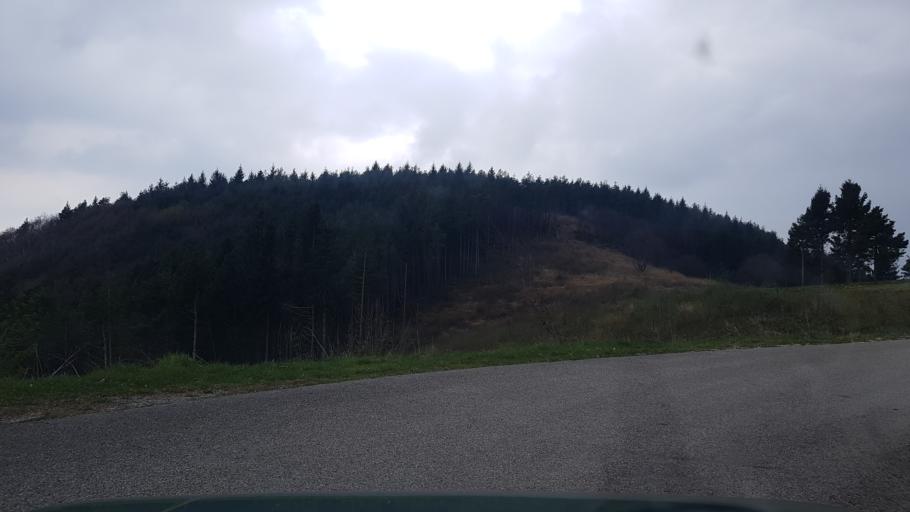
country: IT
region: Friuli Venezia Giulia
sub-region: Provincia di Udine
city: Torreano
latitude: 46.1688
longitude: 13.4125
